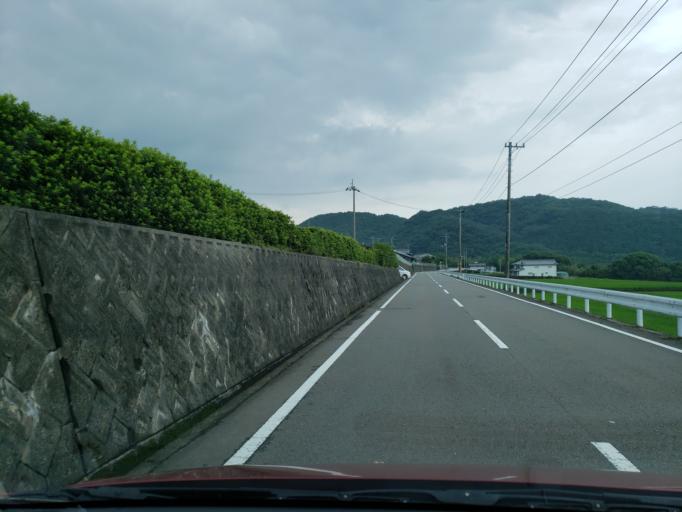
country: JP
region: Tokushima
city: Kamojimacho-jogejima
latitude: 34.1077
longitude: 134.2822
